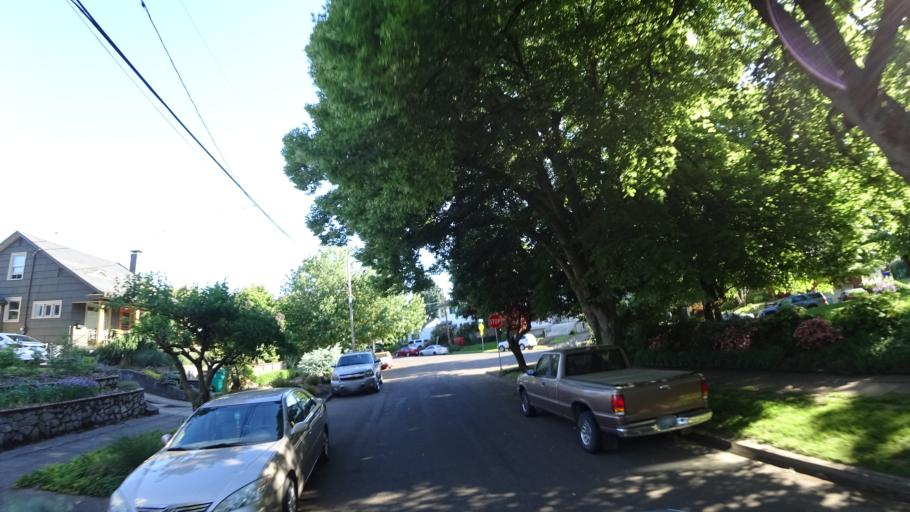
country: US
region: Oregon
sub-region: Multnomah County
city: Portland
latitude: 45.5502
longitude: -122.6841
